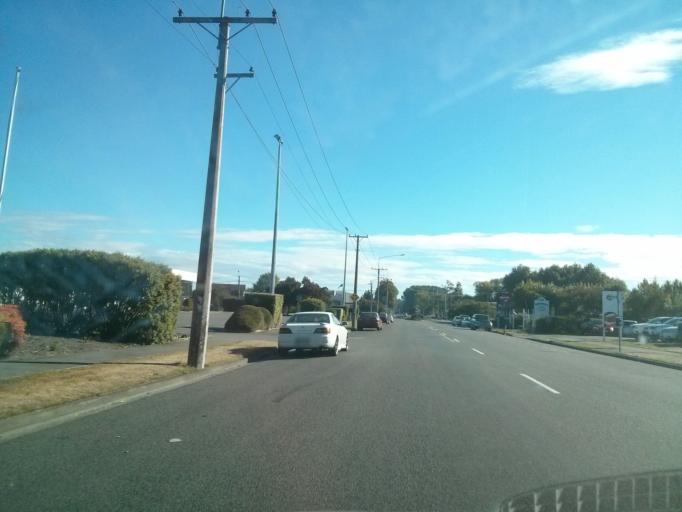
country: NZ
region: Canterbury
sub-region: Christchurch City
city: Christchurch
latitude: -43.4905
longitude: 172.5655
